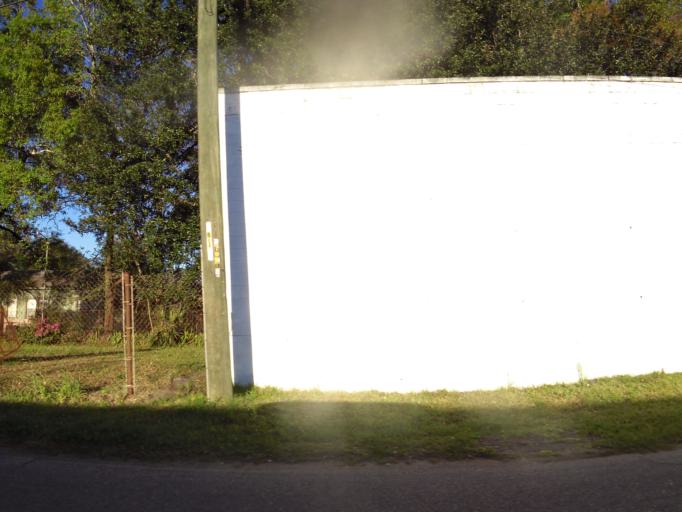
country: US
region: Florida
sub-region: Duval County
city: Jacksonville
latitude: 30.3340
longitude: -81.6983
